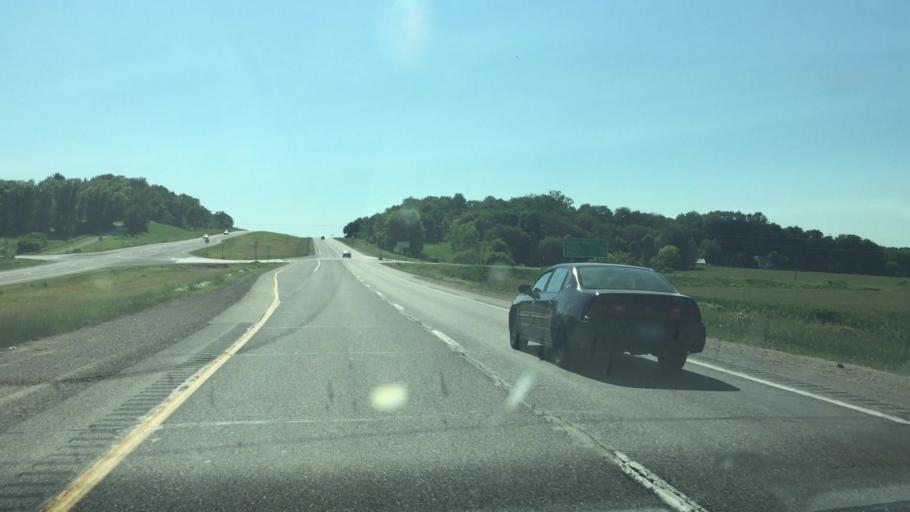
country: US
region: Iowa
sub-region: Linn County
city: Ely
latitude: 41.9261
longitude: -91.5534
